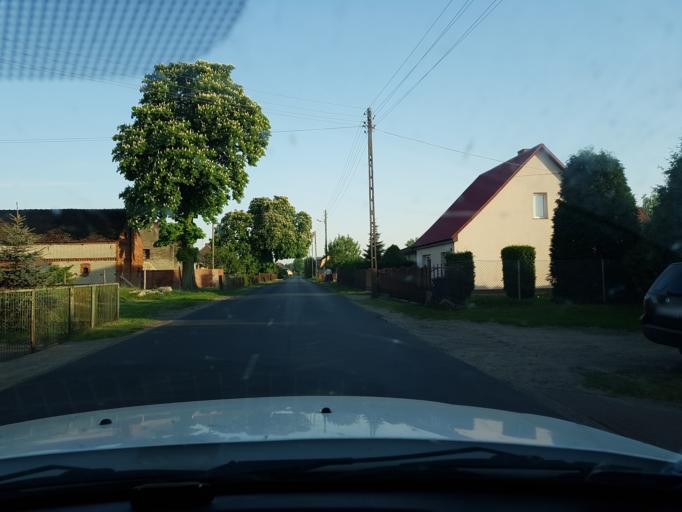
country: PL
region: West Pomeranian Voivodeship
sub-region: Powiat stargardzki
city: Kobylanka
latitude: 53.4247
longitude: 14.9023
